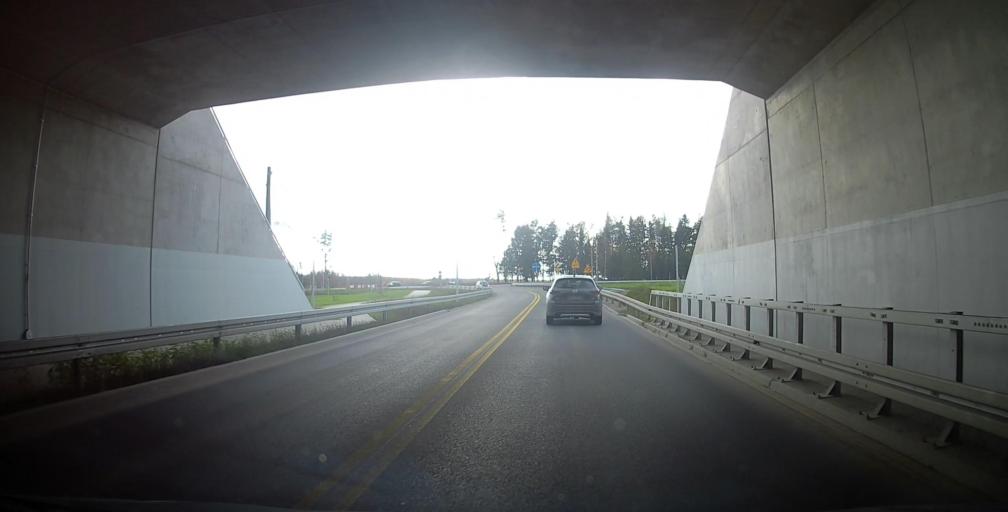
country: PL
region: Warmian-Masurian Voivodeship
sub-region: Powiat elcki
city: Elk
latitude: 53.8394
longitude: 22.4171
